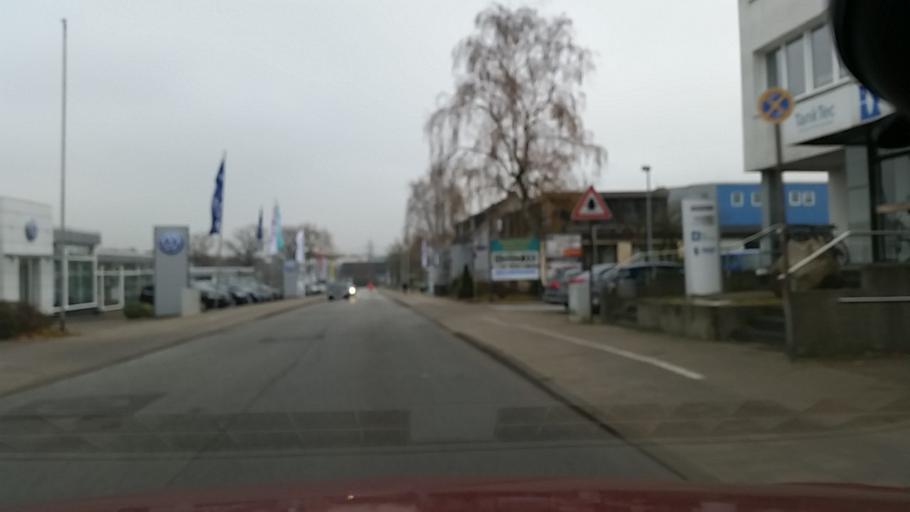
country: DE
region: Schleswig-Holstein
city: Wedel
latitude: 53.5821
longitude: 9.7294
